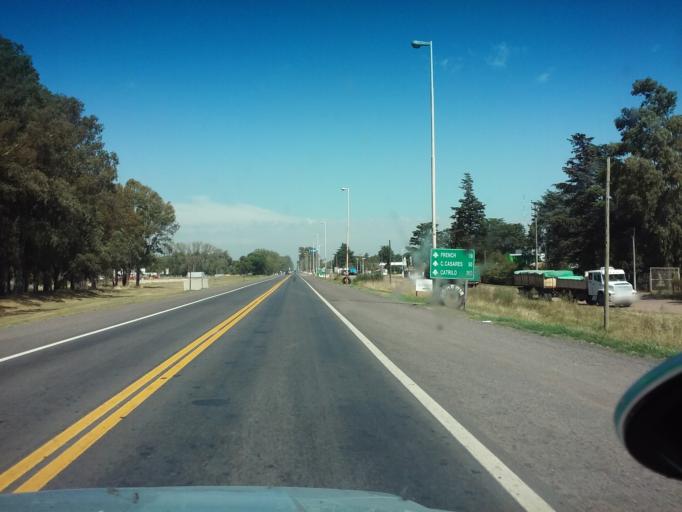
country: AR
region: Buenos Aires
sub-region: Partido de Nueve de Julio
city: Nueve de Julio
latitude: -35.4744
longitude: -60.8619
